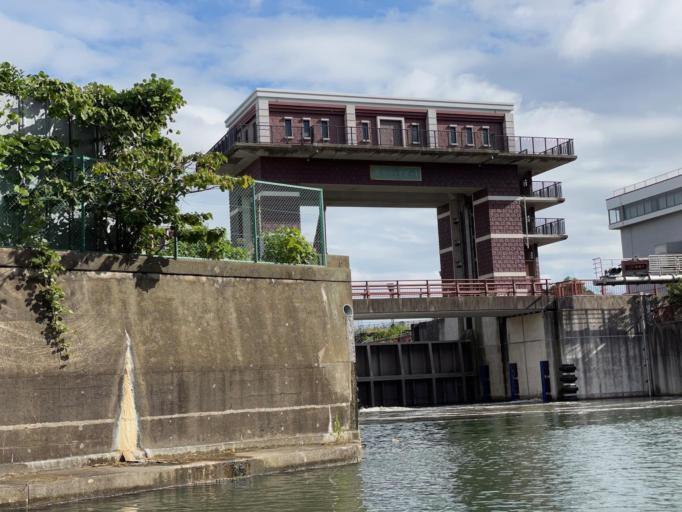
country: JP
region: Tokyo
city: Urayasu
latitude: 35.6841
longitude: 139.8460
